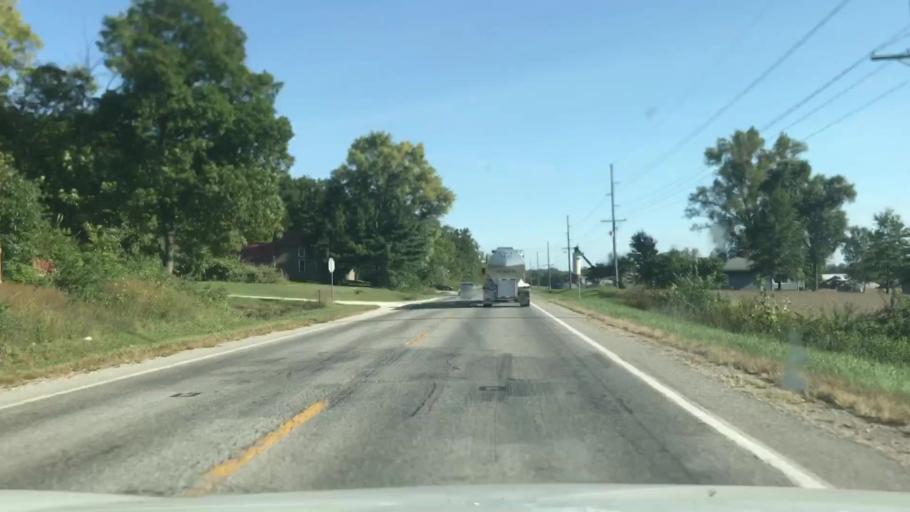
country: US
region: Illinois
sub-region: Adams County
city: Quincy
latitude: 39.8528
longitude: -91.3819
